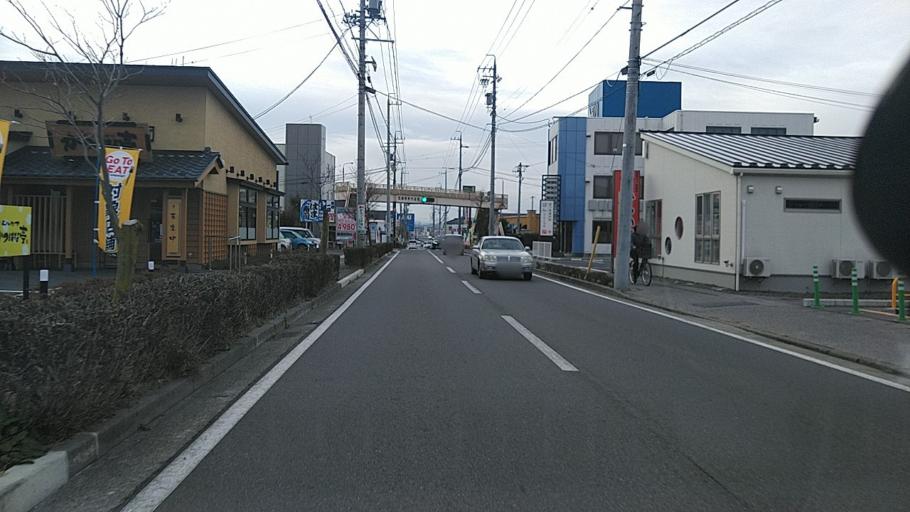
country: JP
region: Nagano
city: Matsumoto
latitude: 36.2249
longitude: 137.9796
